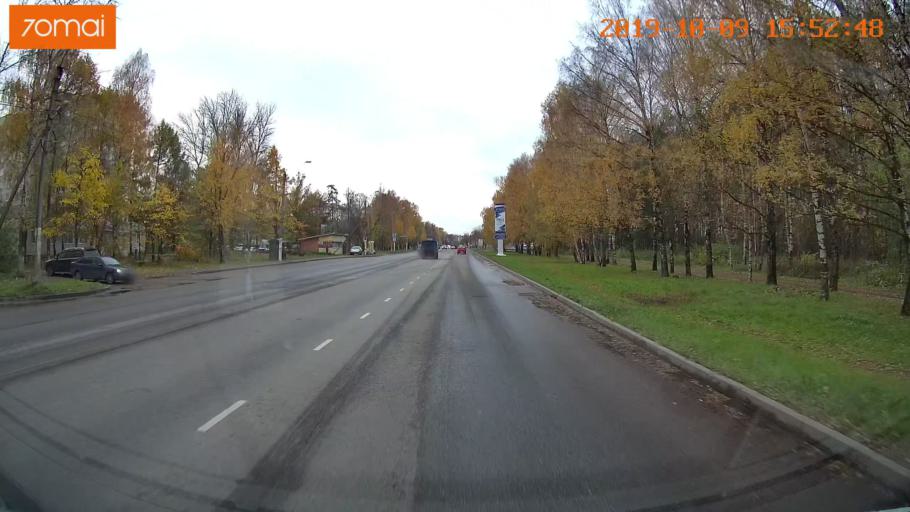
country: RU
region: Kostroma
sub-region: Kostromskoy Rayon
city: Kostroma
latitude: 57.7868
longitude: 40.9637
